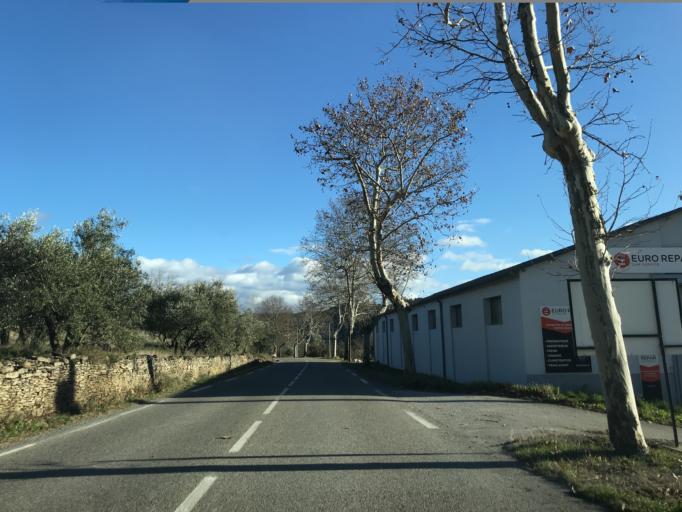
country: FR
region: Rhone-Alpes
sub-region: Departement de l'Ardeche
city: Les Vans
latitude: 44.4084
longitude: 4.1130
